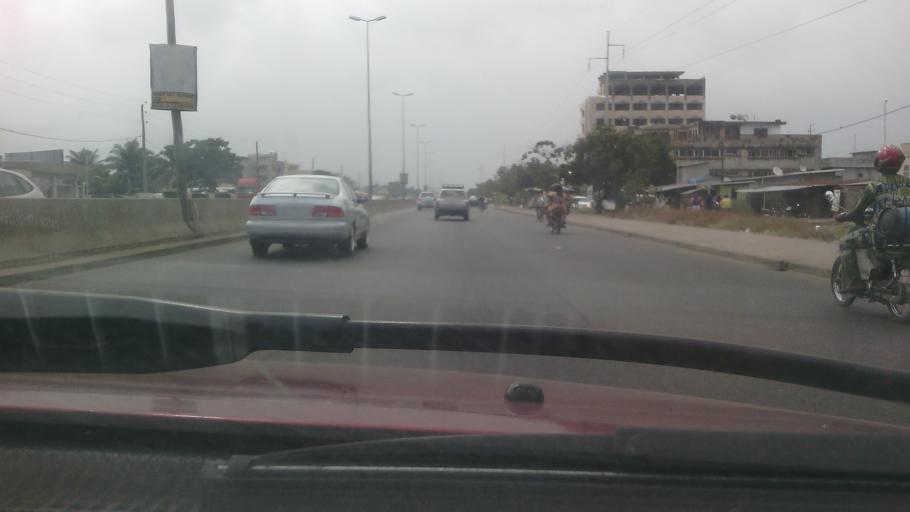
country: BJ
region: Littoral
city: Cotonou
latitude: 6.3693
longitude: 2.4894
